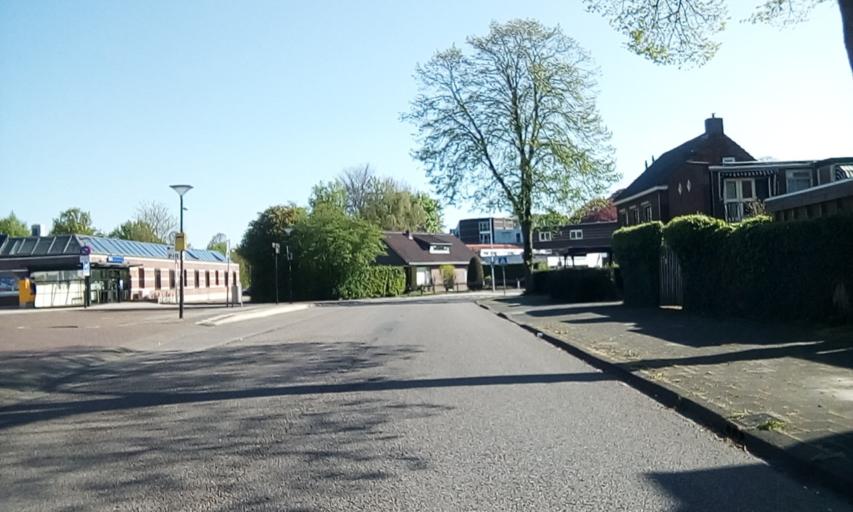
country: NL
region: Gelderland
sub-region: Gemeente Tiel
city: Tiel
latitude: 51.8895
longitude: 5.4237
